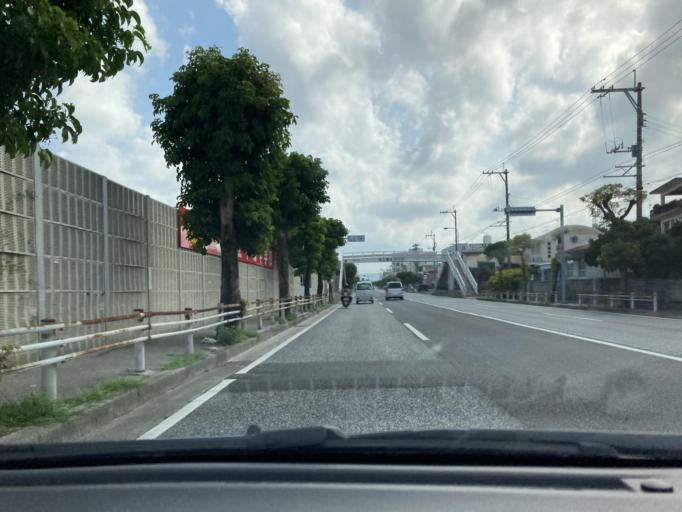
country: JP
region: Okinawa
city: Ginowan
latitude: 26.2689
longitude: 127.7912
